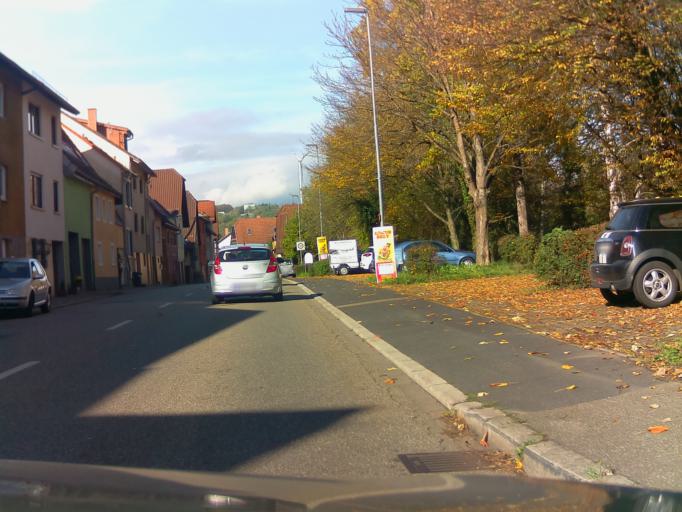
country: DE
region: Baden-Wuerttemberg
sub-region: Karlsruhe Region
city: Joehlingen
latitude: 48.9994
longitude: 8.5309
